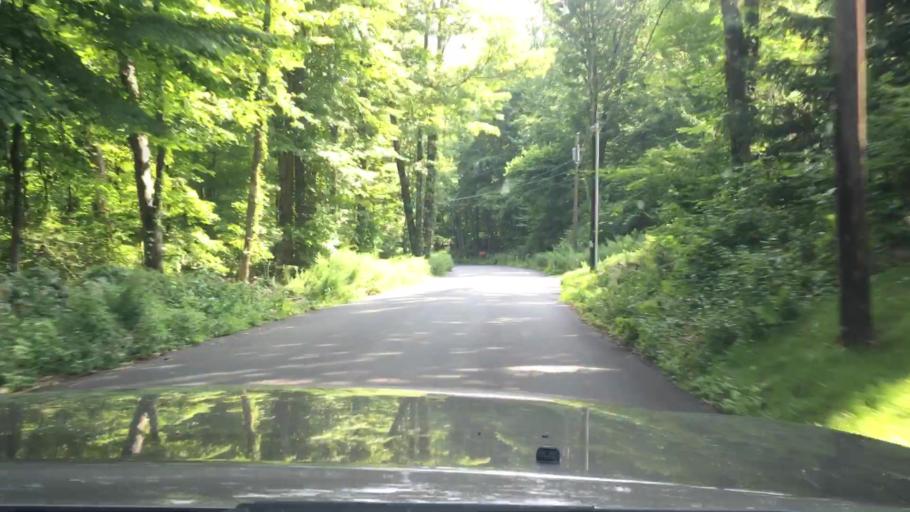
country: US
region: Connecticut
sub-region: Fairfield County
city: Georgetown
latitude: 41.2663
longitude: -73.4533
